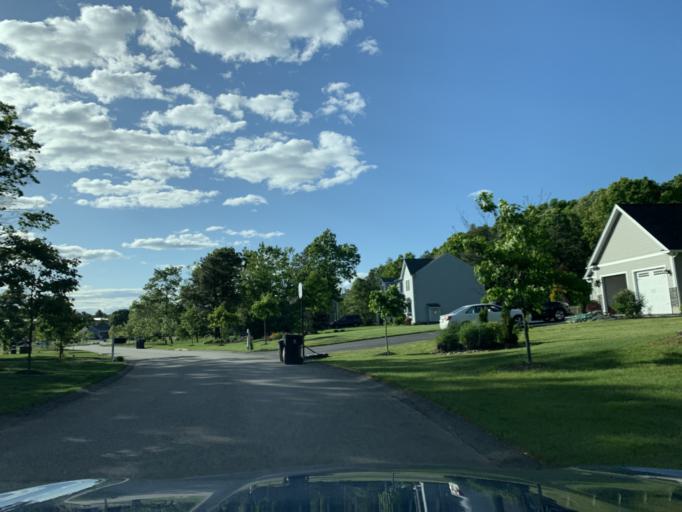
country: US
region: Rhode Island
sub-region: Kent County
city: East Greenwich
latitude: 41.6314
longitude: -71.4611
